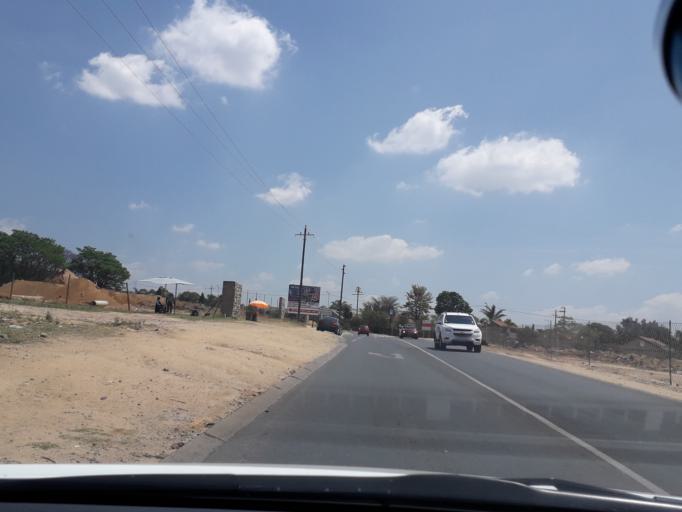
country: ZA
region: Gauteng
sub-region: City of Johannesburg Metropolitan Municipality
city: Midrand
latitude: -26.0090
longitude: 28.0788
